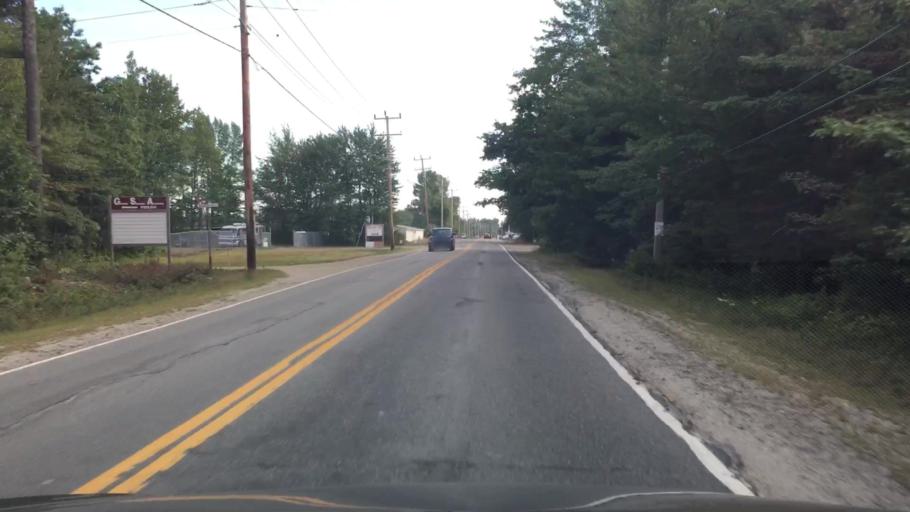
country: US
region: Maine
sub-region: Hancock County
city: Surry
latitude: 44.4327
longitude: -68.5741
